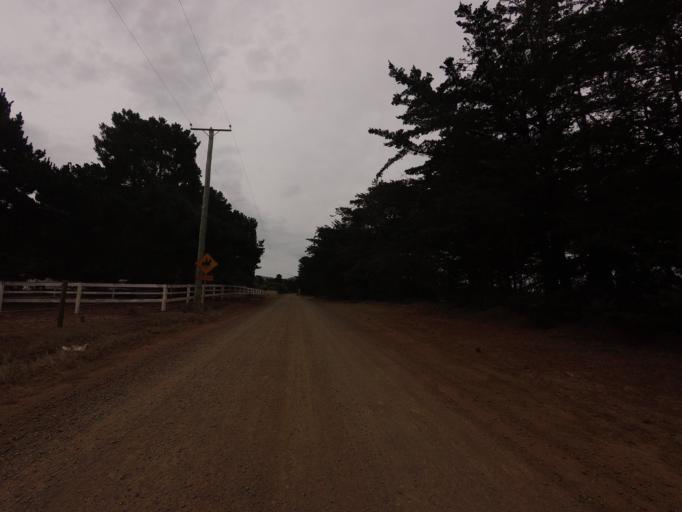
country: AU
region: Tasmania
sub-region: Clarence
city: Seven Mile Beach
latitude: -42.8356
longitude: 147.5313
